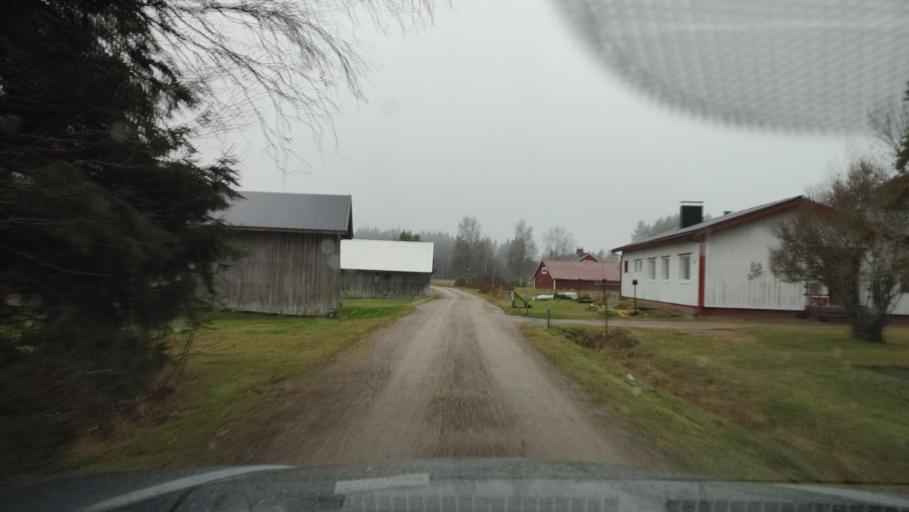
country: FI
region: Southern Ostrobothnia
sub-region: Suupohja
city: Karijoki
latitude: 62.1896
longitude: 21.7736
